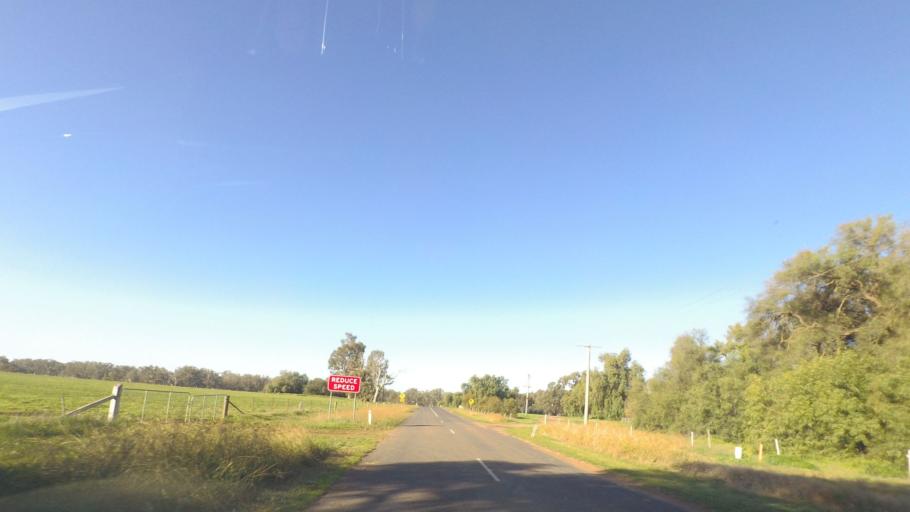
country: AU
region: Victoria
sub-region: Greater Bendigo
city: Epsom
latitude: -36.6466
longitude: 144.5383
